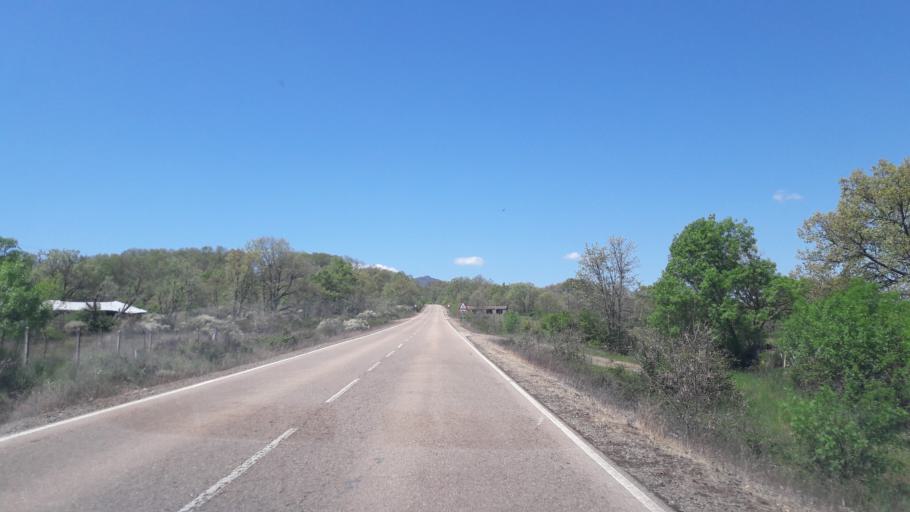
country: ES
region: Castille and Leon
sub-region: Provincia de Salamanca
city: Linares de Riofrio
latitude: 40.5915
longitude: -5.8892
